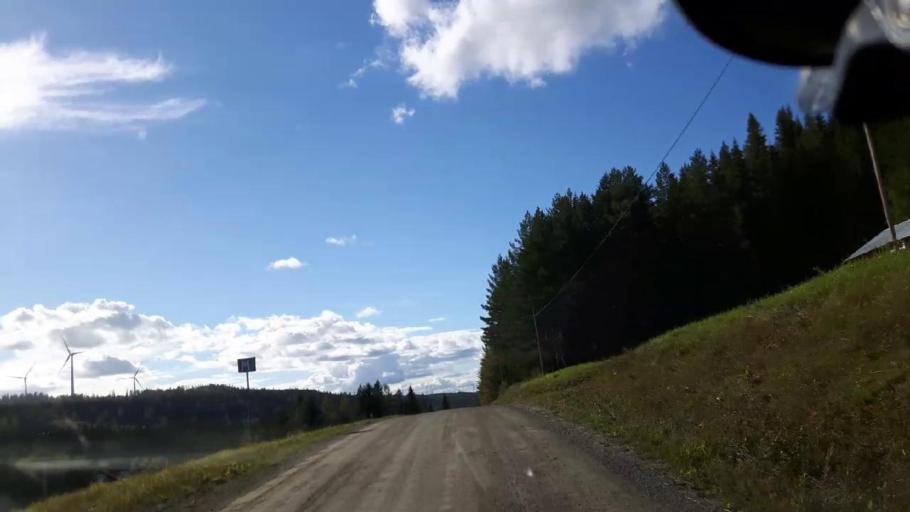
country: SE
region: Jaemtland
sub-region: Ragunda Kommun
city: Hammarstrand
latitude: 63.4763
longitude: 16.1590
